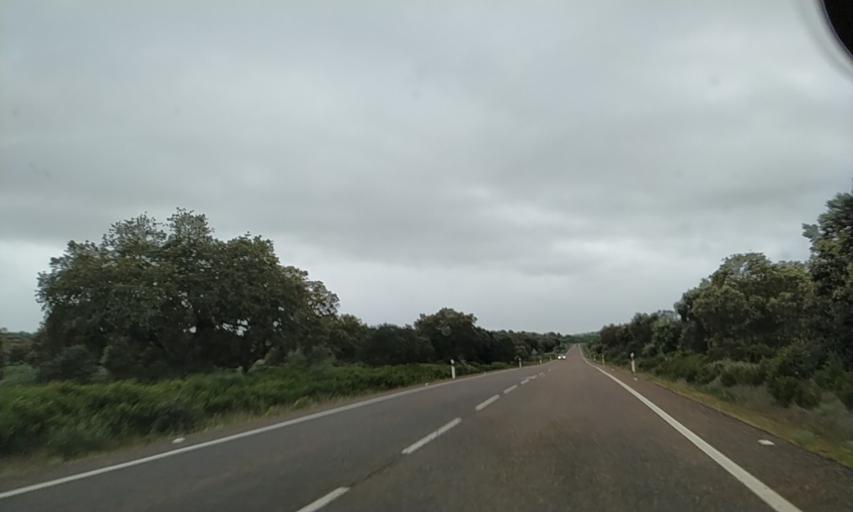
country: ES
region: Extremadura
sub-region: Provincia de Badajoz
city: La Roca de la Sierra
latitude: 39.1237
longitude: -6.6700
